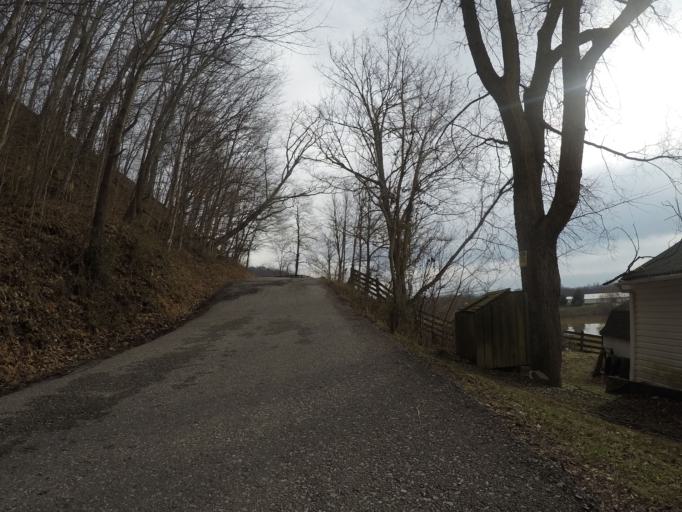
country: US
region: West Virginia
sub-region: Cabell County
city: Huntington
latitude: 38.4392
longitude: -82.4634
